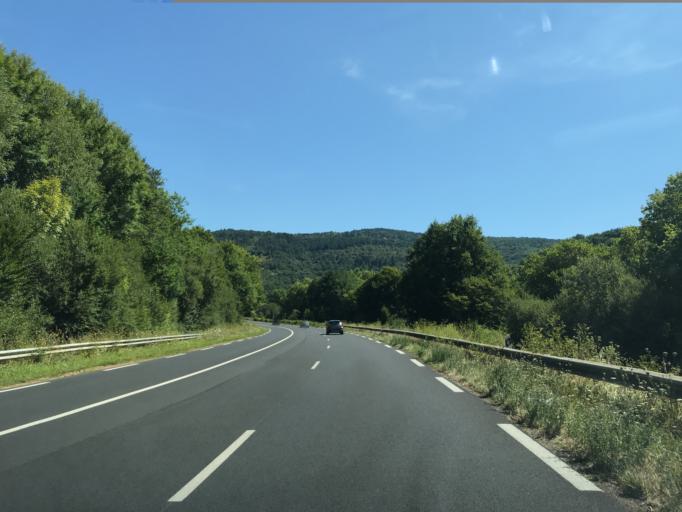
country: FR
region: Limousin
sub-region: Departement de la Correze
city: Cornil
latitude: 45.1801
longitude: 1.6514
